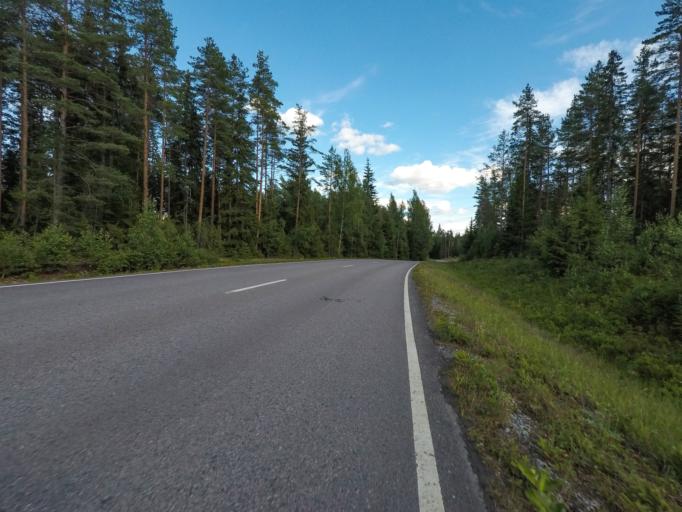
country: FI
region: South Karelia
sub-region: Lappeenranta
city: Joutseno
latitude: 61.1455
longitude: 28.6254
